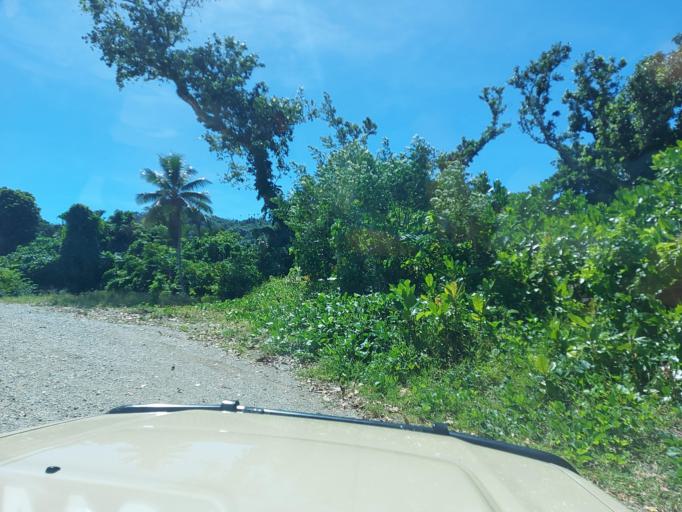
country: VU
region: Penama
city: Saratamata
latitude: -15.9588
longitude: 168.1930
